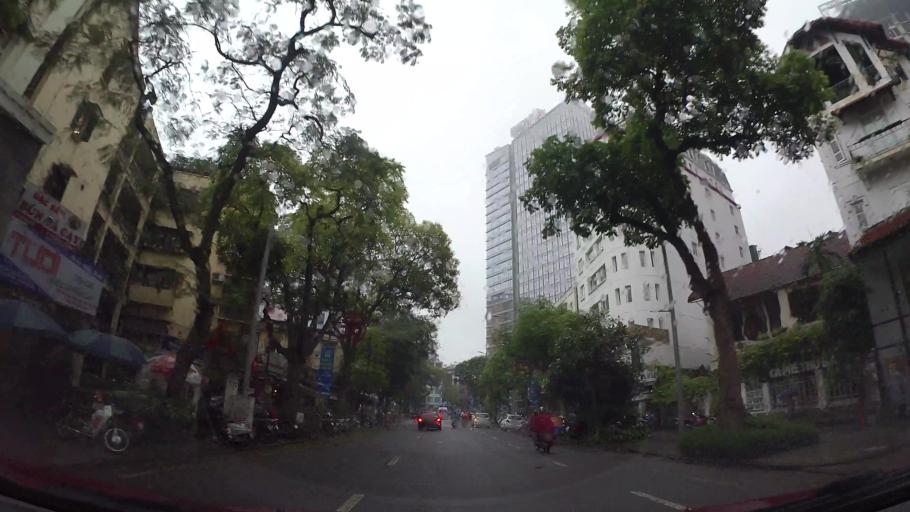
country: VN
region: Ha Noi
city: Hoan Kiem
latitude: 21.0284
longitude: 105.8563
